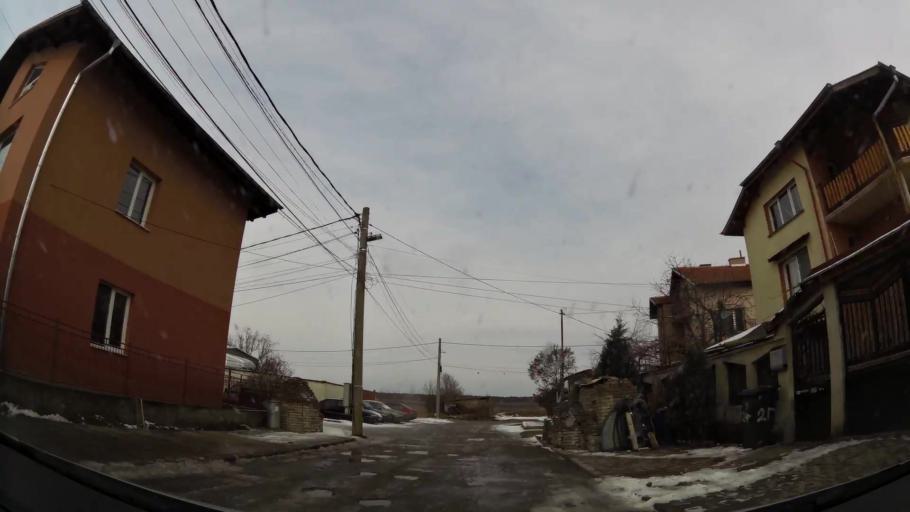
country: BG
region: Sofia-Capital
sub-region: Stolichna Obshtina
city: Sofia
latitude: 42.7162
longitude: 23.4097
